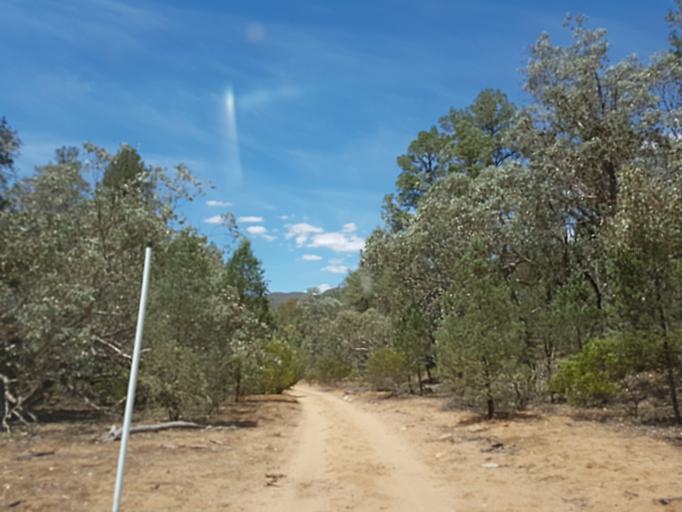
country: AU
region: New South Wales
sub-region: Snowy River
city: Jindabyne
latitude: -36.9437
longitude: 148.3913
